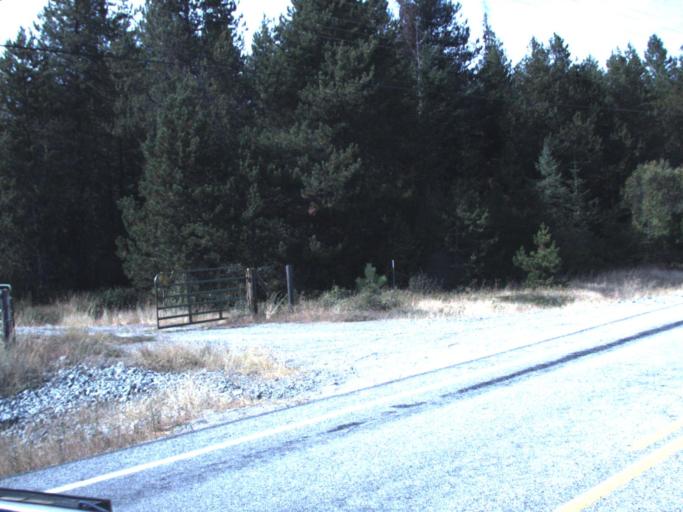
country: US
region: Washington
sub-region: Pend Oreille County
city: Newport
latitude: 48.2547
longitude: -117.2845
